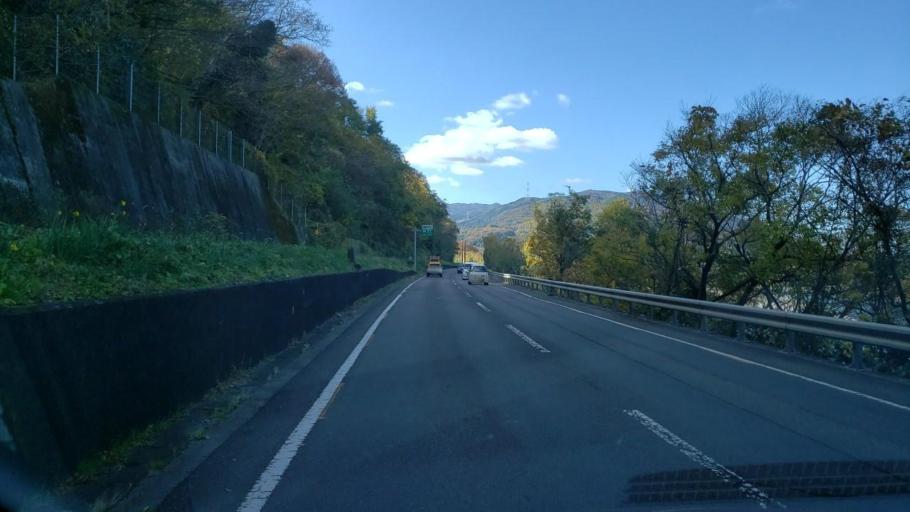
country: JP
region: Tokushima
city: Wakimachi
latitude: 34.0597
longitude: 134.1853
